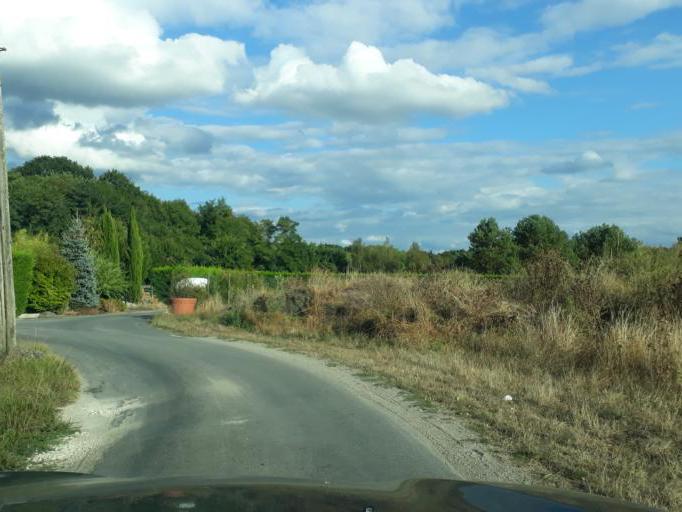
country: FR
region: Centre
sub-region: Departement du Loiret
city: Trainou
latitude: 47.9745
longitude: 2.1183
